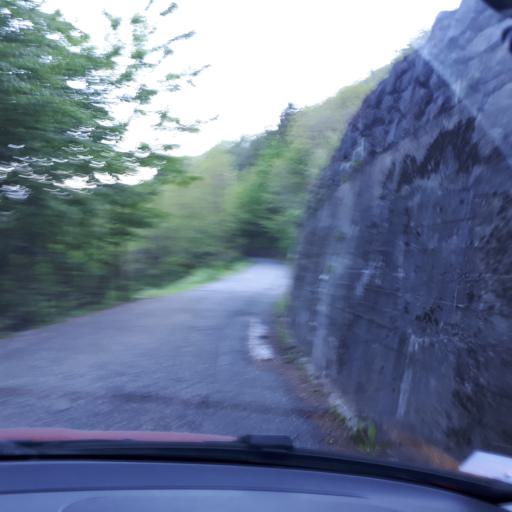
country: IT
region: Lombardy
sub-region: Provincia di Como
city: Musso
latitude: 46.1129
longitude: 9.2686
